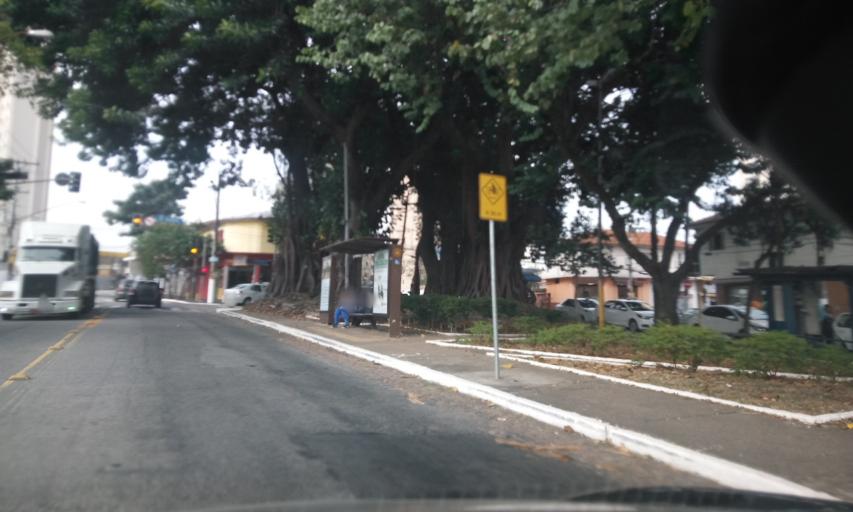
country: BR
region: Sao Paulo
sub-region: Sao Caetano Do Sul
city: Sao Caetano do Sul
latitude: -23.6173
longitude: -46.6060
